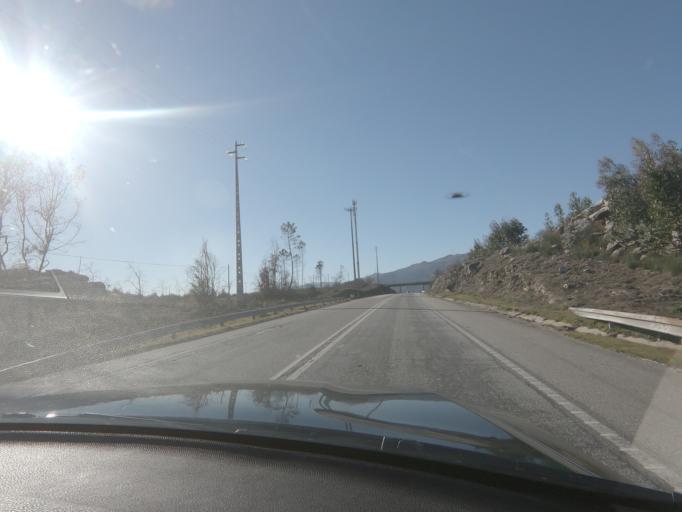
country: PT
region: Viseu
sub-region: Vouzela
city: Vouzela
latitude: 40.6468
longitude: -8.0542
